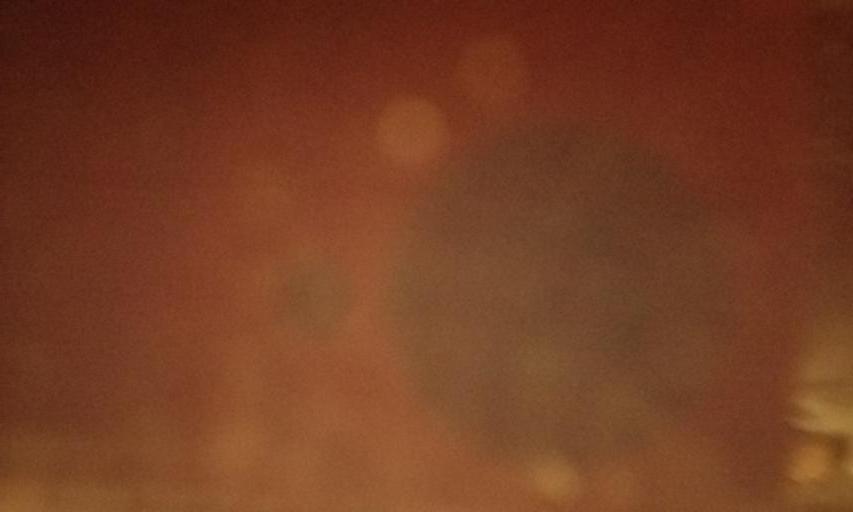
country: JP
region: Okayama
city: Kasaoka
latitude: 34.5265
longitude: 133.4839
